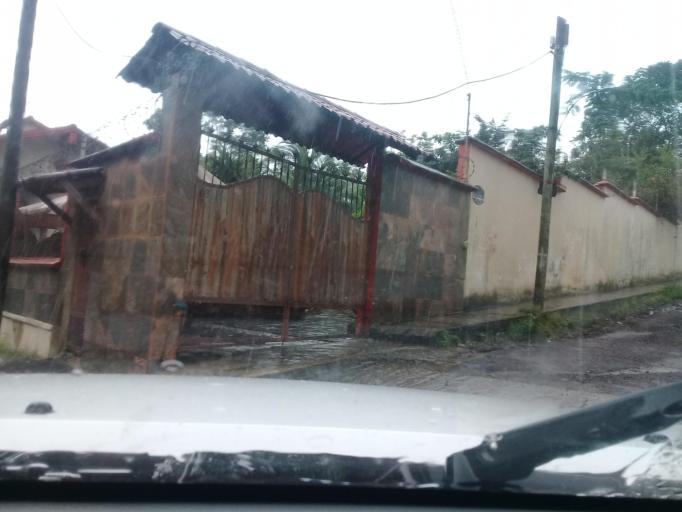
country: MX
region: Veracruz
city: Santiago Tuxtla
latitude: 18.4592
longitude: -95.3130
